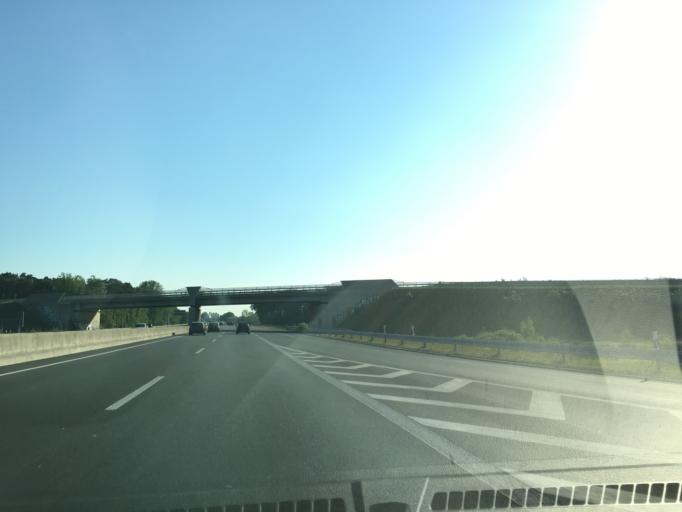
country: DE
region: North Rhine-Westphalia
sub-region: Regierungsbezirk Munster
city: Ladbergen
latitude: 52.1127
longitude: 7.6989
